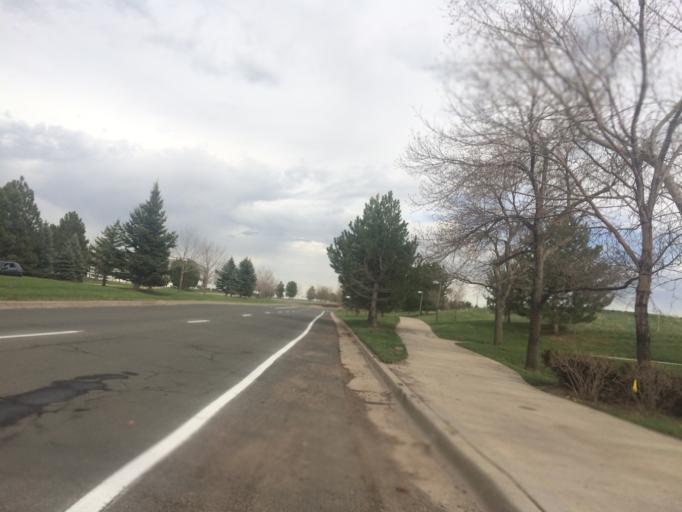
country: US
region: Colorado
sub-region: Broomfield County
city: Broomfield
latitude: 39.9197
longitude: -105.1083
